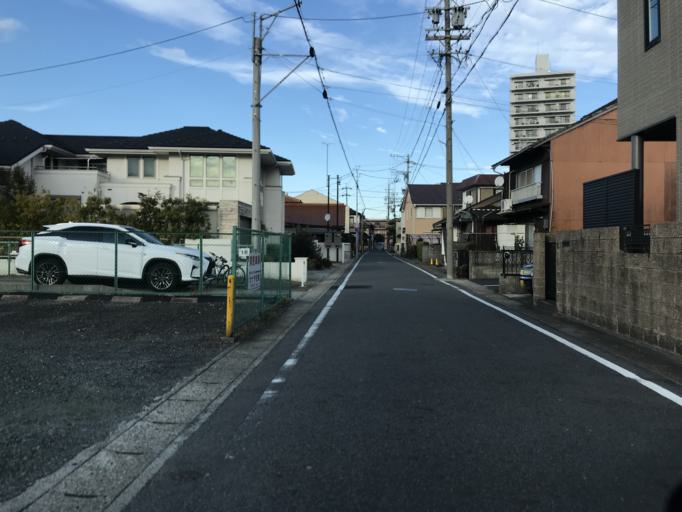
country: JP
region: Aichi
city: Nagoya-shi
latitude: 35.1963
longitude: 136.8669
